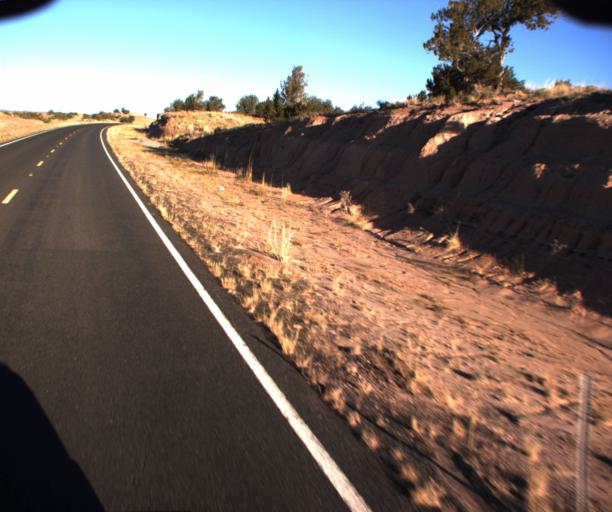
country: US
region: Arizona
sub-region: Apache County
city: Houck
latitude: 35.3782
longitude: -109.4910
